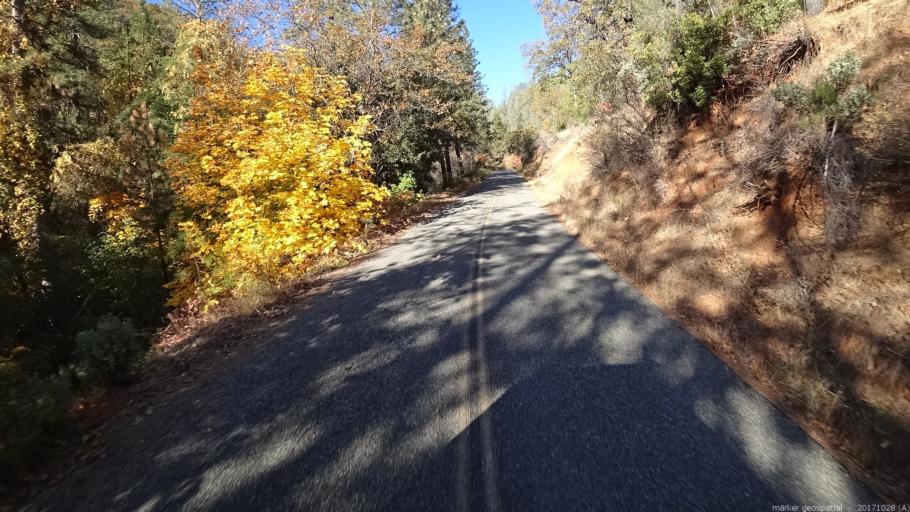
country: US
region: California
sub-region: Trinity County
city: Lewiston
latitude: 40.6504
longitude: -122.6724
